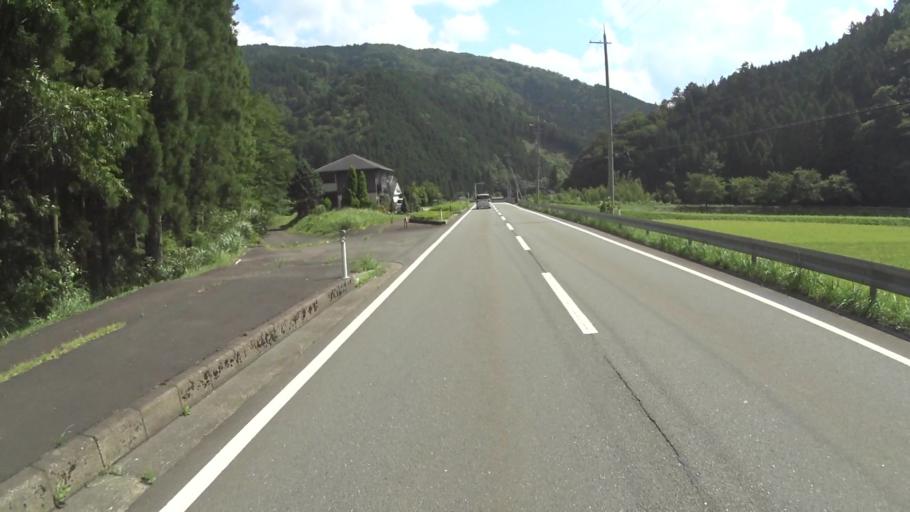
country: JP
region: Fukui
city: Obama
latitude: 35.3257
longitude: 135.5655
